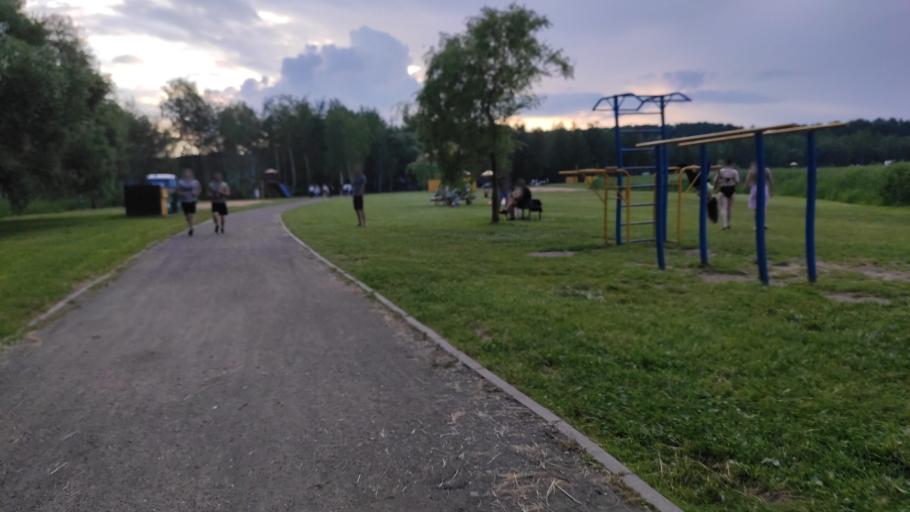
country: BY
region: Minsk
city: Zhdanovichy
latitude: 53.9561
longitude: 27.4484
